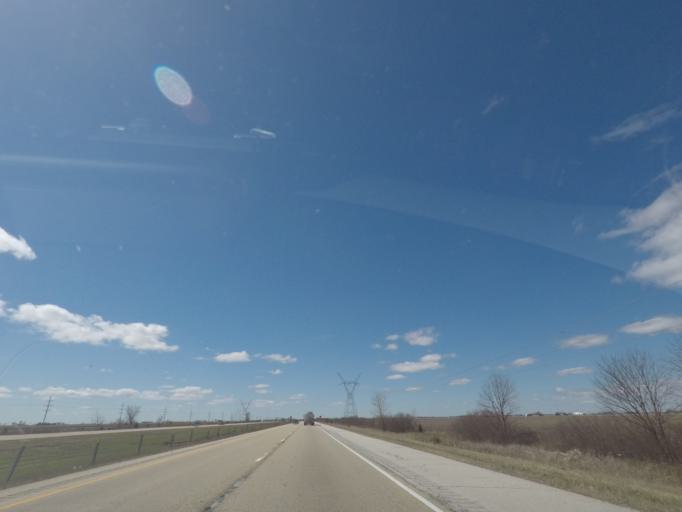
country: US
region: Illinois
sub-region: Livingston County
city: Dwight
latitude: 41.1395
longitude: -88.3704
